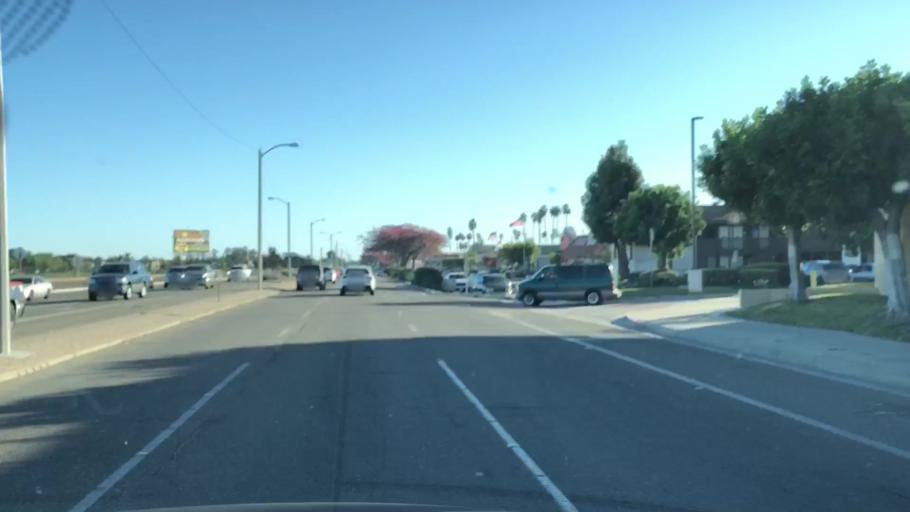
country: US
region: California
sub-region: Ventura County
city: Oxnard
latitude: 34.2189
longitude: -119.1772
